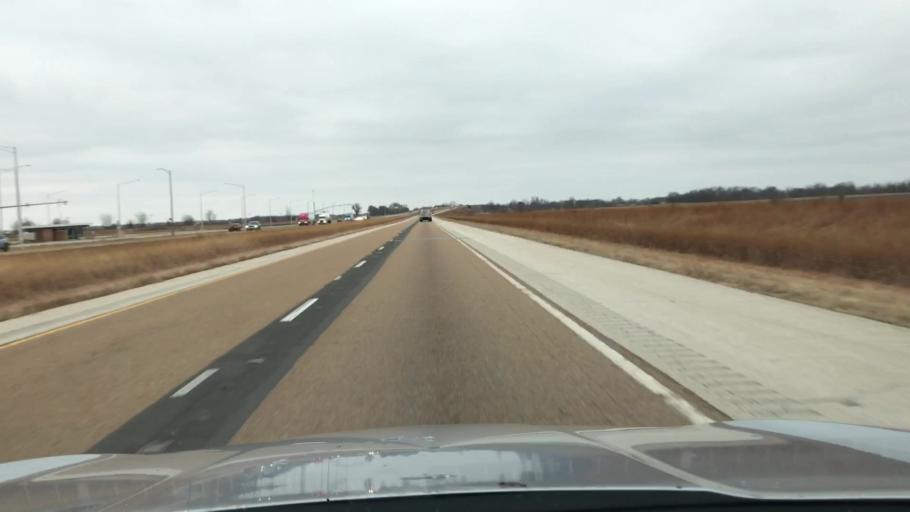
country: US
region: Illinois
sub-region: Montgomery County
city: Litchfield
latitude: 39.2291
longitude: -89.6438
